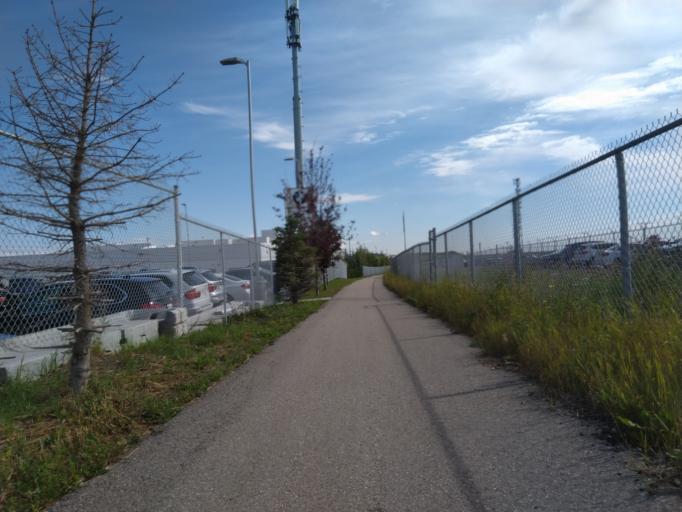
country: CA
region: Alberta
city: Calgary
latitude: 51.1517
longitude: -114.1953
